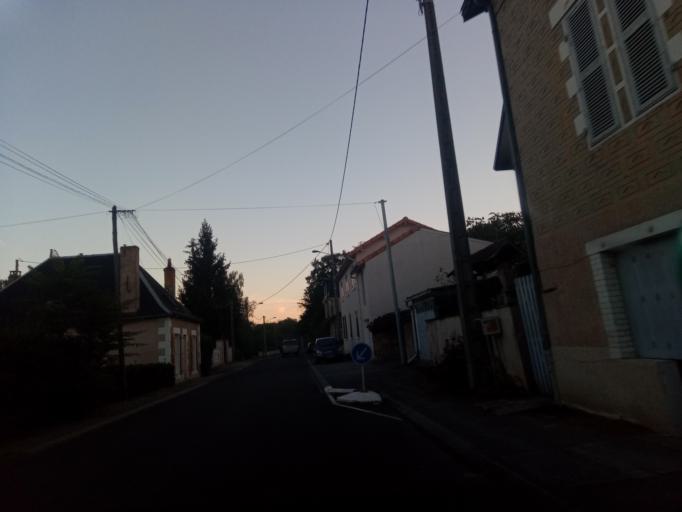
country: FR
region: Poitou-Charentes
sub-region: Departement de la Vienne
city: Montmorillon
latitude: 46.4098
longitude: 0.8802
